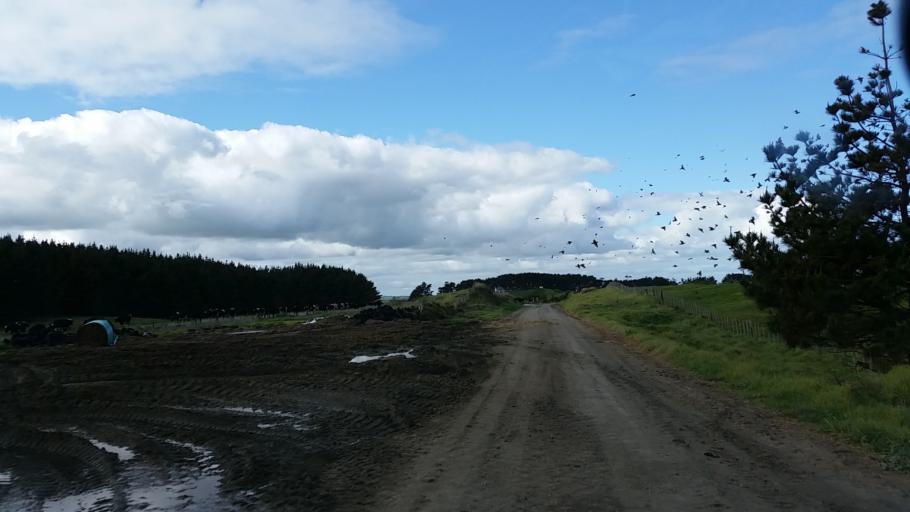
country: NZ
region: Taranaki
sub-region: South Taranaki District
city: Patea
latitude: -39.8003
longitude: 174.5995
